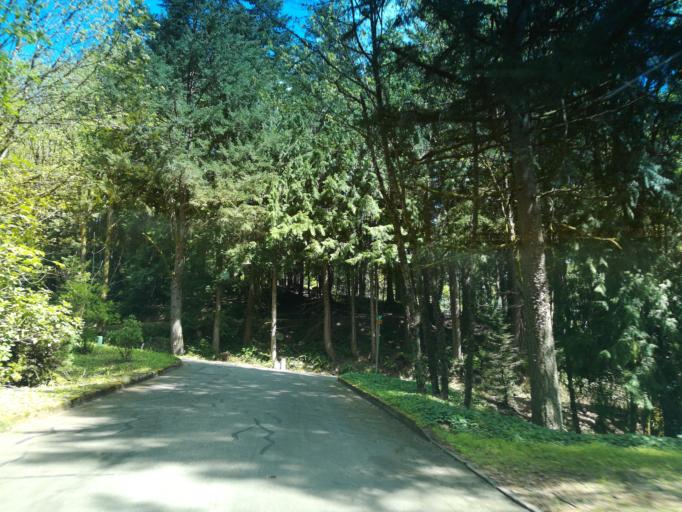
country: US
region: Oregon
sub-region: Multnomah County
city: Gresham
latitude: 45.4553
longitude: -122.4276
